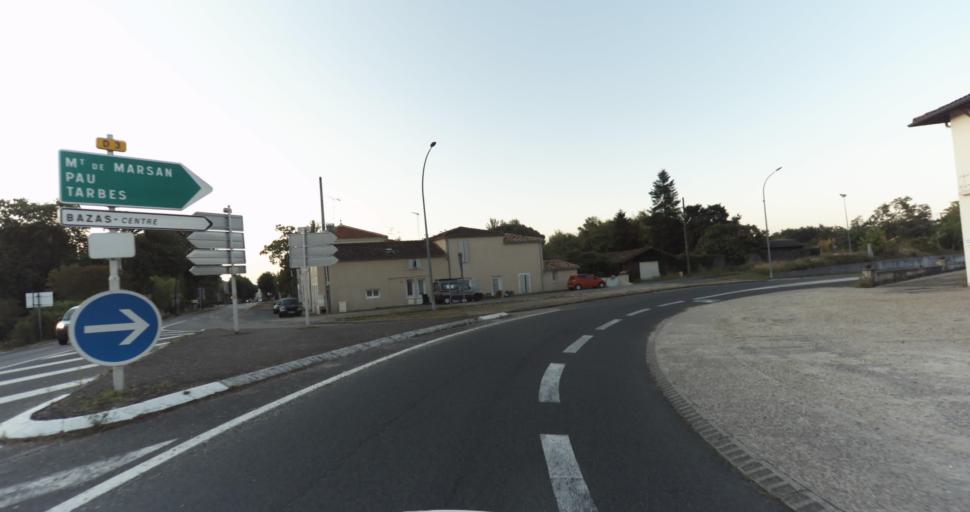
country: FR
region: Aquitaine
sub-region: Departement de la Gironde
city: Bazas
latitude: 44.4351
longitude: -0.2193
